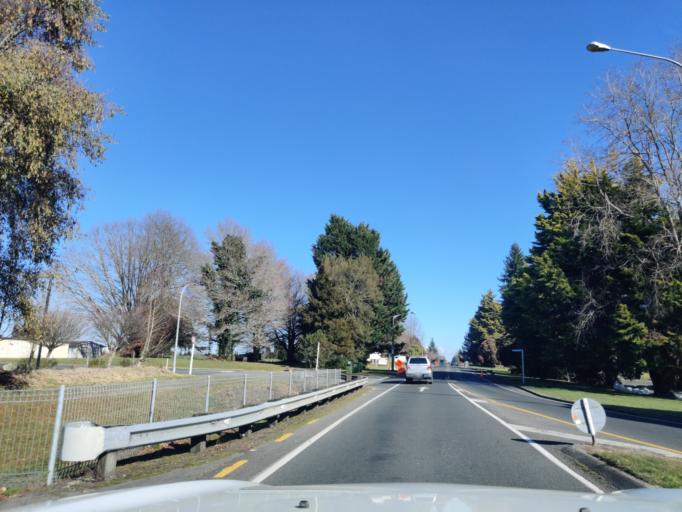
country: NZ
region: Waikato
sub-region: South Waikato District
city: Tokoroa
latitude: -38.2264
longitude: 175.8768
